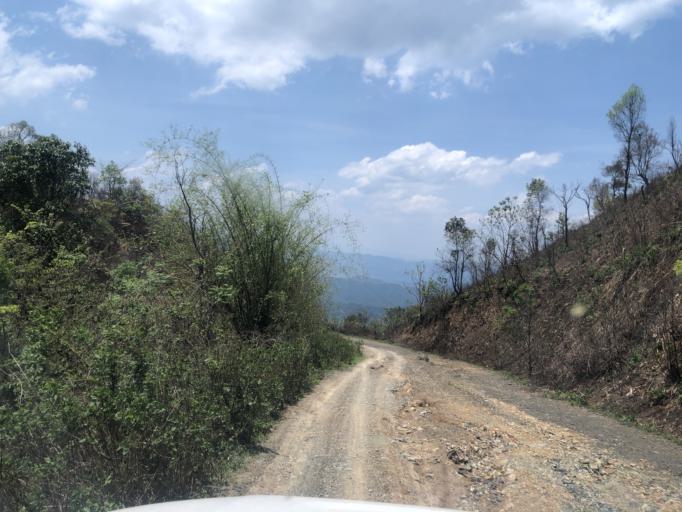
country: LA
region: Phongsali
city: Phongsali
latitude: 21.4333
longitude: 102.1609
